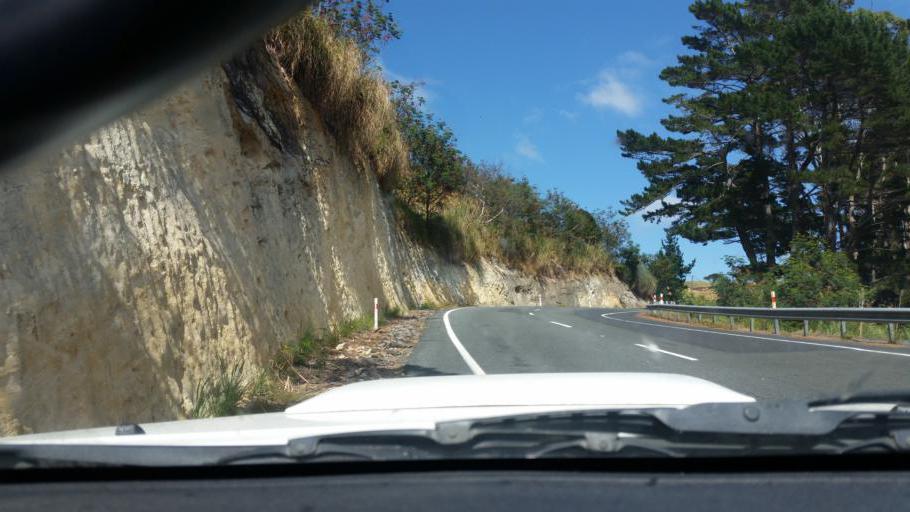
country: NZ
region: Northland
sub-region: Kaipara District
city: Dargaville
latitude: -35.8227
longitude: 173.6924
